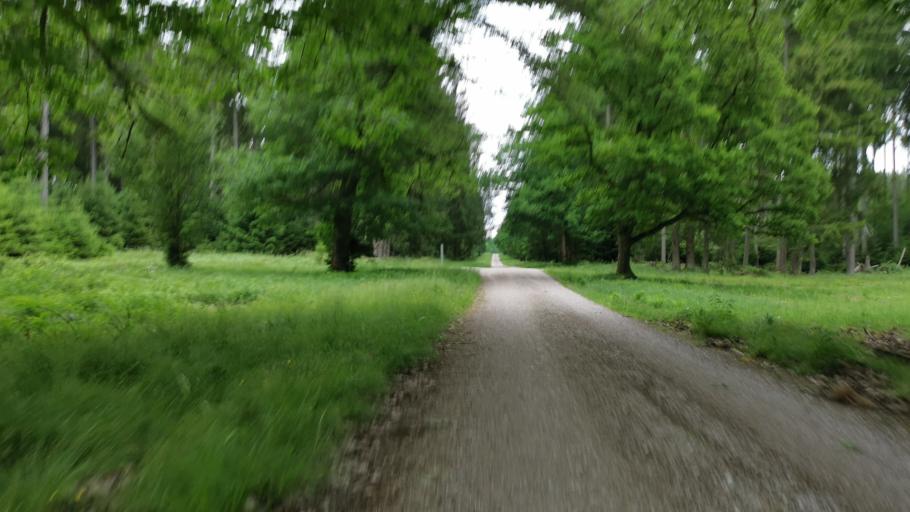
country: DE
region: Bavaria
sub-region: Upper Bavaria
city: Baierbrunn
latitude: 48.0343
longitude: 11.4586
